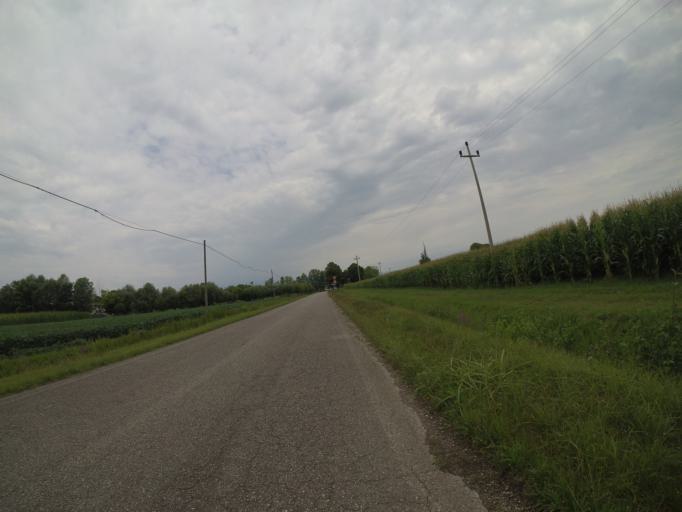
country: IT
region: Friuli Venezia Giulia
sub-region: Provincia di Udine
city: Camino al Tagliamento
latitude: 45.9182
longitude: 12.9537
